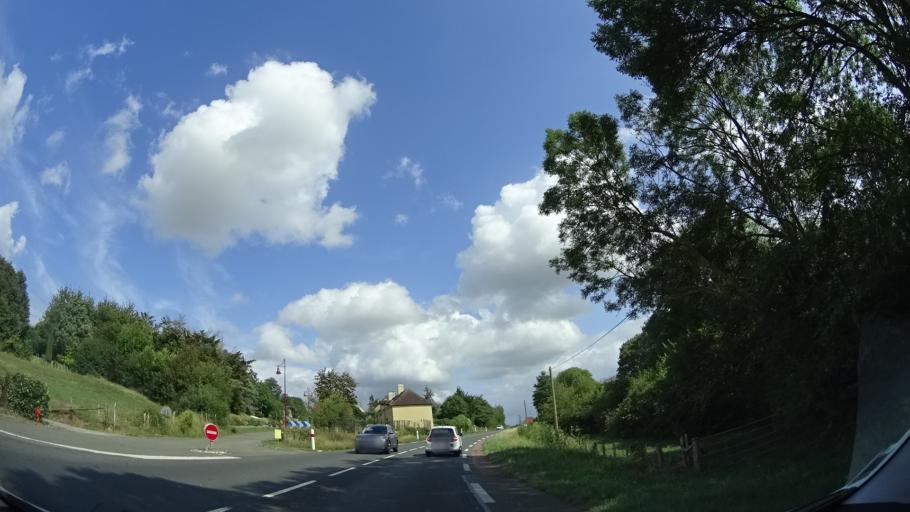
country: FR
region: Pays de la Loire
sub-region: Departement de la Sarthe
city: Coulans-sur-Gee
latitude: 48.0185
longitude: 0.0019
